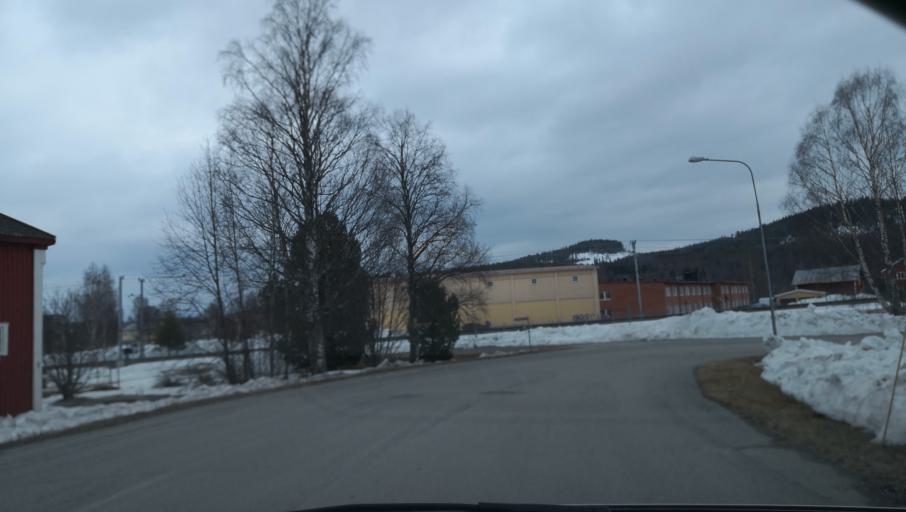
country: SE
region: Vaesterbotten
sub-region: Vannas Kommun
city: Vannasby
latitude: 63.9158
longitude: 19.8146
